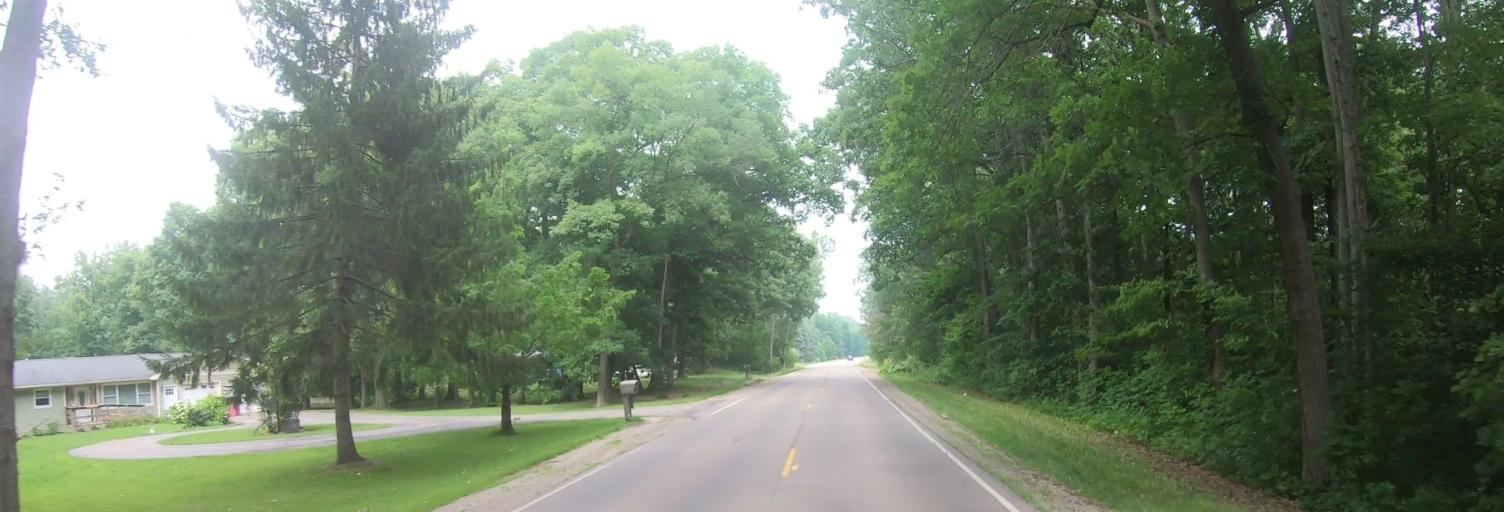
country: US
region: Michigan
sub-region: Shiawassee County
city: Corunna
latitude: 42.8703
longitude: -84.1039
